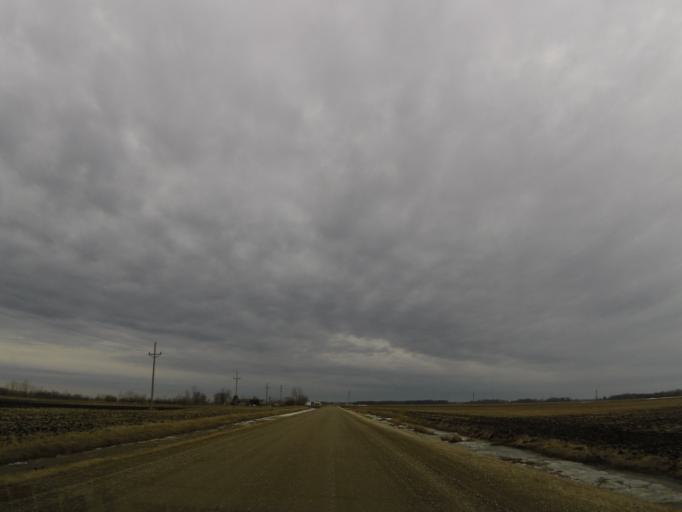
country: US
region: North Dakota
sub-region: Walsh County
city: Grafton
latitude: 48.4198
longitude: -97.4440
